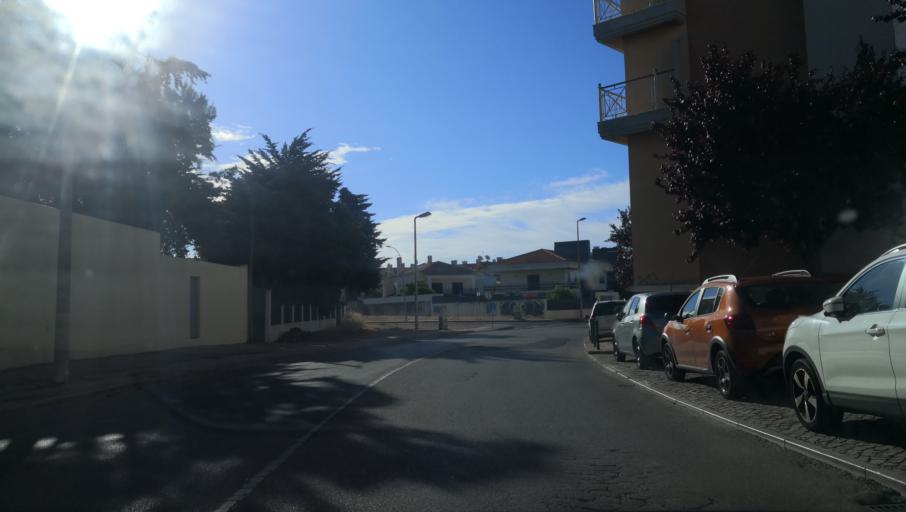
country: PT
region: Lisbon
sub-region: Oeiras
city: Carcavelos
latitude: 38.6847
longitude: -9.3265
